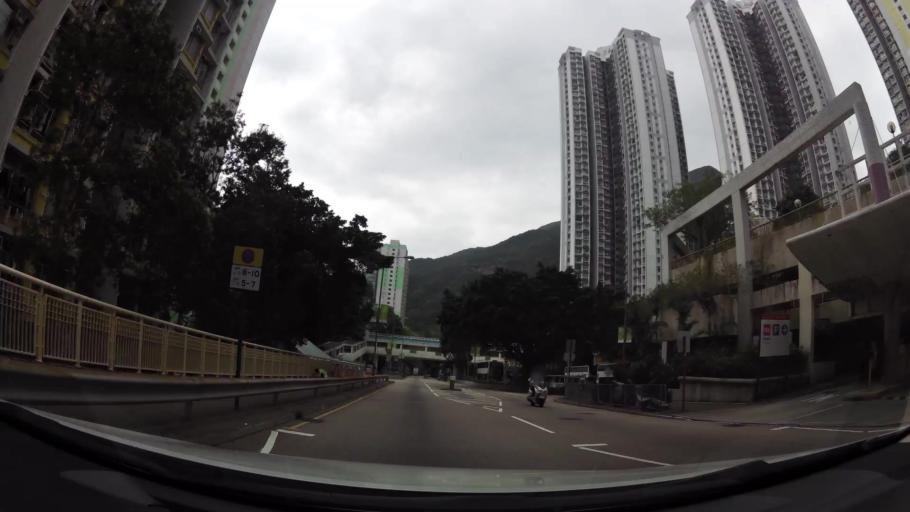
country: HK
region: Wanchai
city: Wan Chai
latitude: 22.2786
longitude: 114.2227
